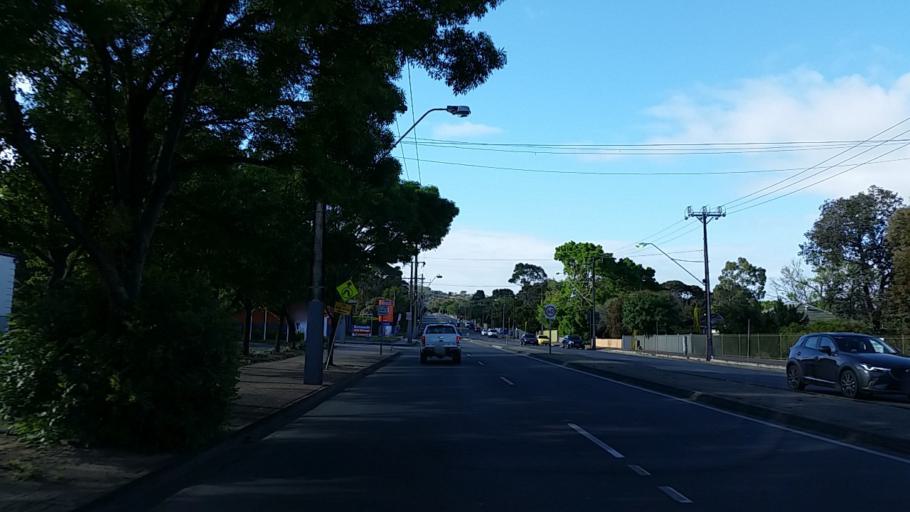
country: AU
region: South Australia
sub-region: Mitcham
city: Clapham
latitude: -34.9921
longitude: 138.5928
